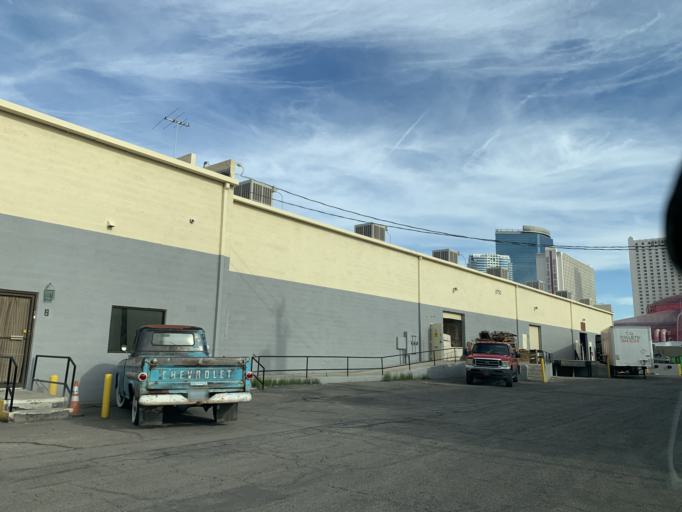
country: US
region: Nevada
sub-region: Clark County
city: Paradise
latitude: 36.1395
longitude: -115.1702
